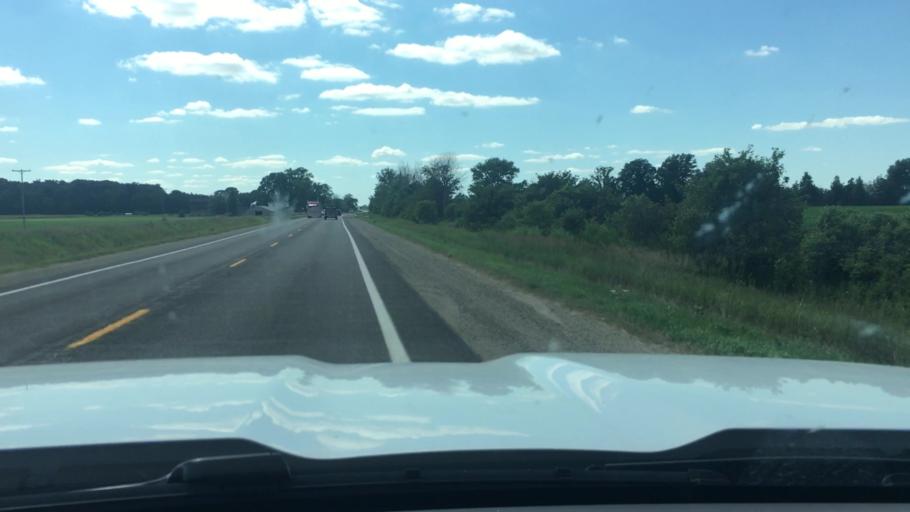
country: US
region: Michigan
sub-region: Gratiot County
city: Ithaca
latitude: 43.1757
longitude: -84.4802
